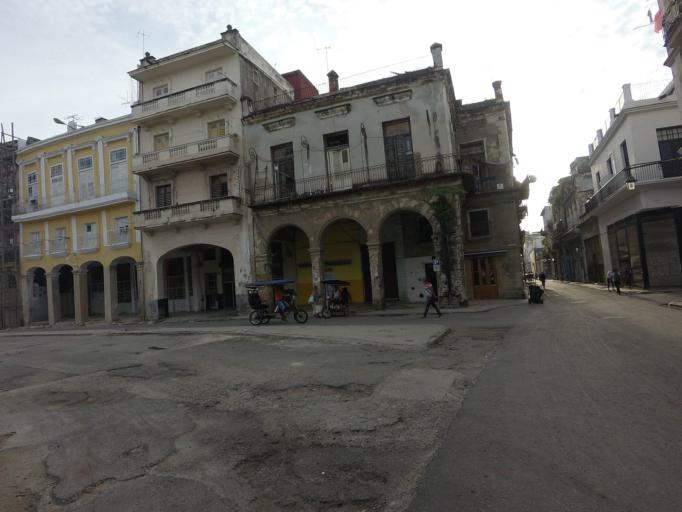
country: CU
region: La Habana
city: La Habana Vieja
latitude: 23.1358
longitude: -82.3557
